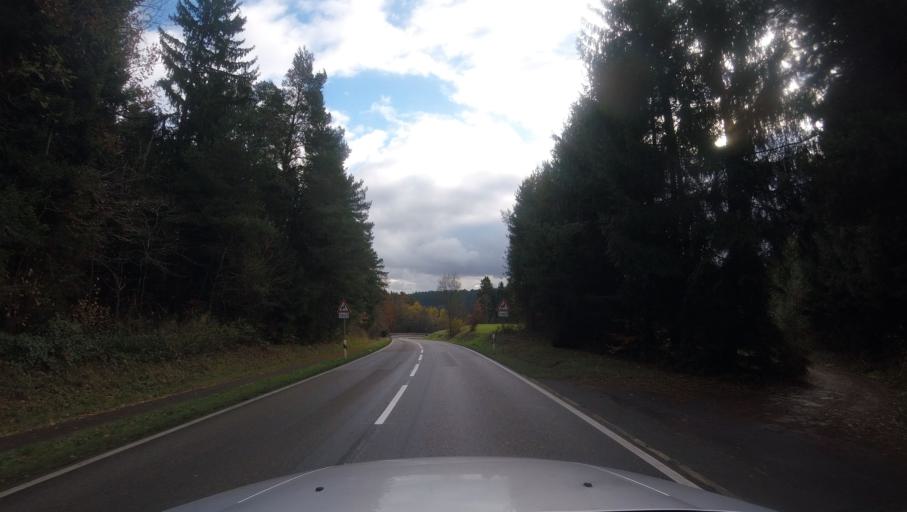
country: DE
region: Baden-Wuerttemberg
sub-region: Regierungsbezirk Stuttgart
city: Spraitbach
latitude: 48.8607
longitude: 9.7637
